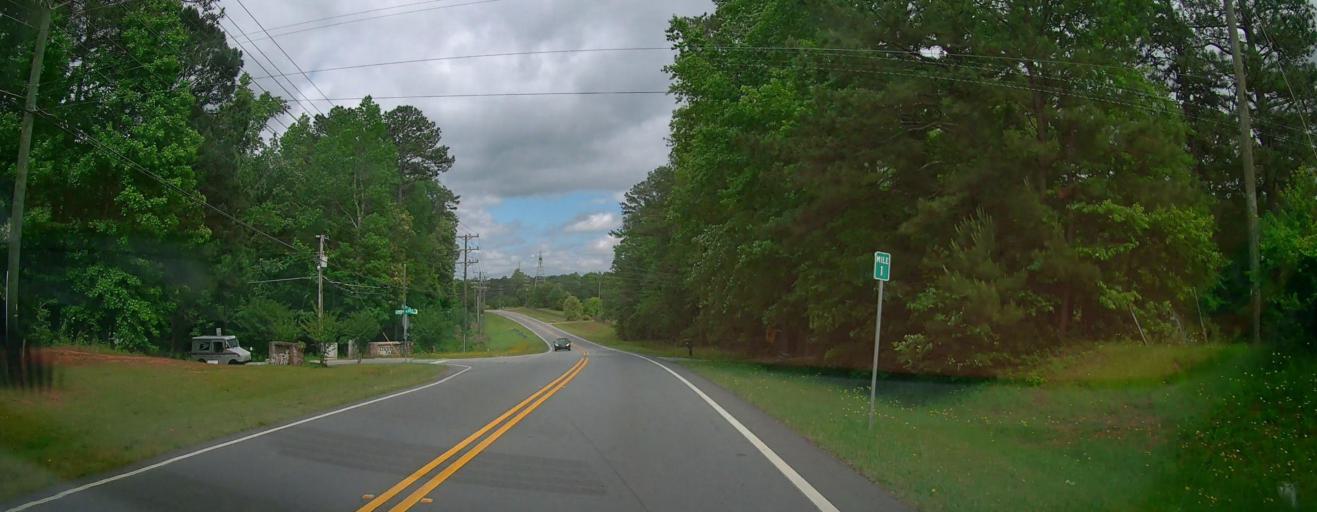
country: US
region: Georgia
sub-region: DeKalb County
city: Pine Mountain
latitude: 33.5928
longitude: -84.1321
